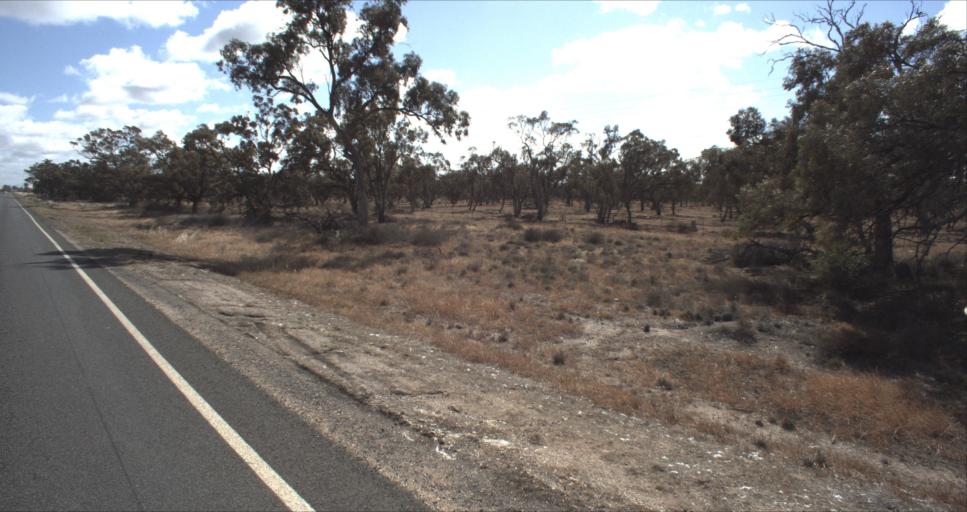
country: AU
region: New South Wales
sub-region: Murrumbidgee Shire
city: Darlington Point
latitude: -34.5249
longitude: 146.1750
